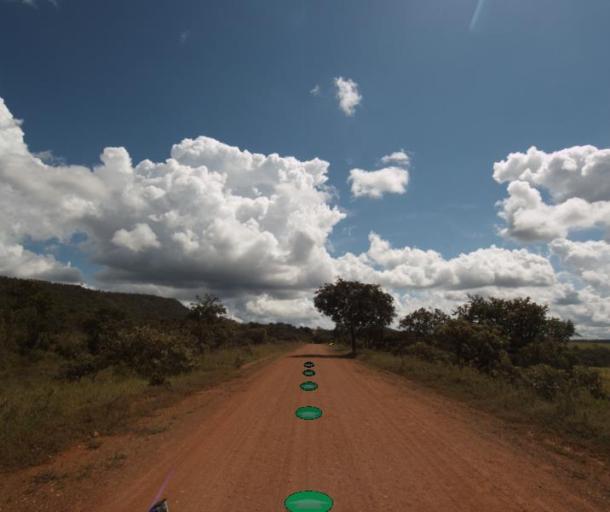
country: BR
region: Goias
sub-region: Pirenopolis
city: Pirenopolis
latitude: -15.7807
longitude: -48.8339
